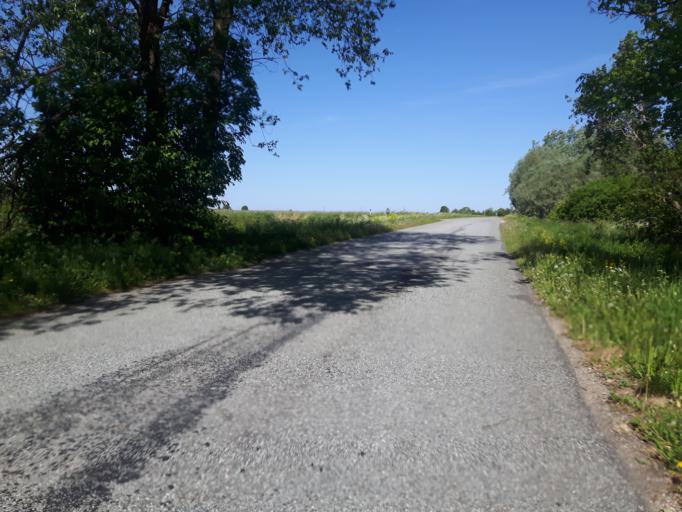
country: EE
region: Ida-Virumaa
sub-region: Aseri vald
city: Aseri
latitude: 59.4654
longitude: 26.8225
